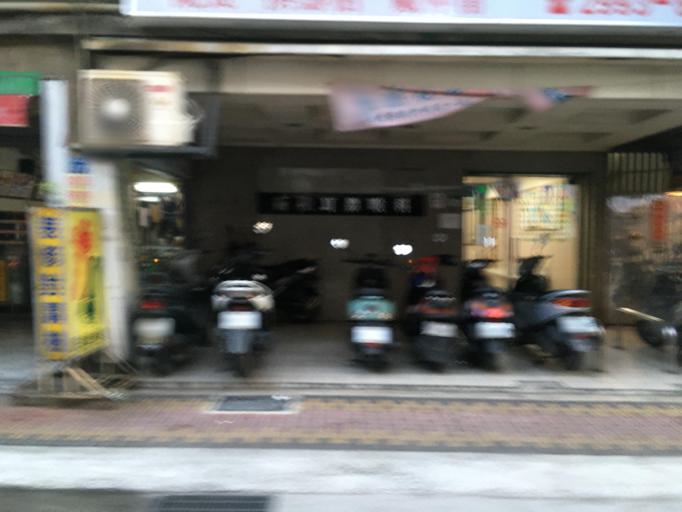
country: TW
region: Taipei
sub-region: Taipei
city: Banqiao
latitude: 25.0495
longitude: 121.4571
